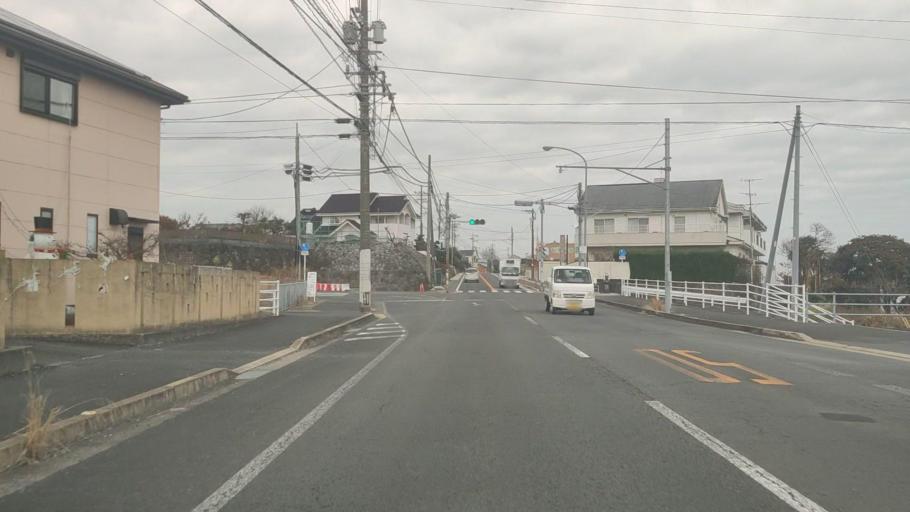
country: JP
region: Nagasaki
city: Shimabara
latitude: 32.8150
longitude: 130.3567
